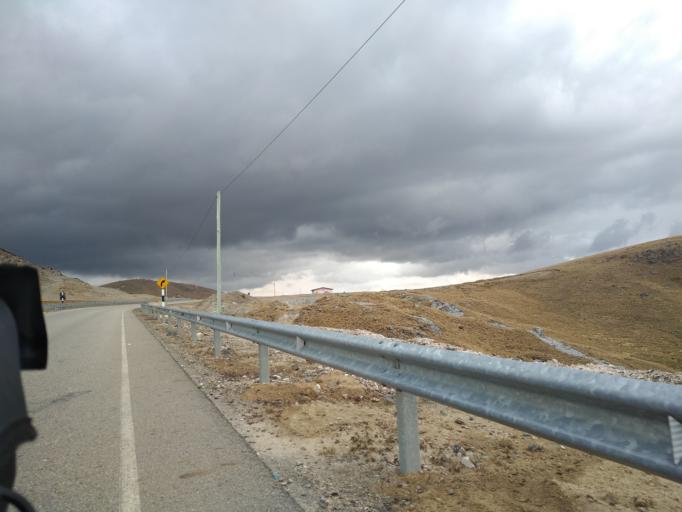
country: PE
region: La Libertad
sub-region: Provincia de Santiago de Chuco
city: Quiruvilca
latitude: -7.9901
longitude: -78.2854
